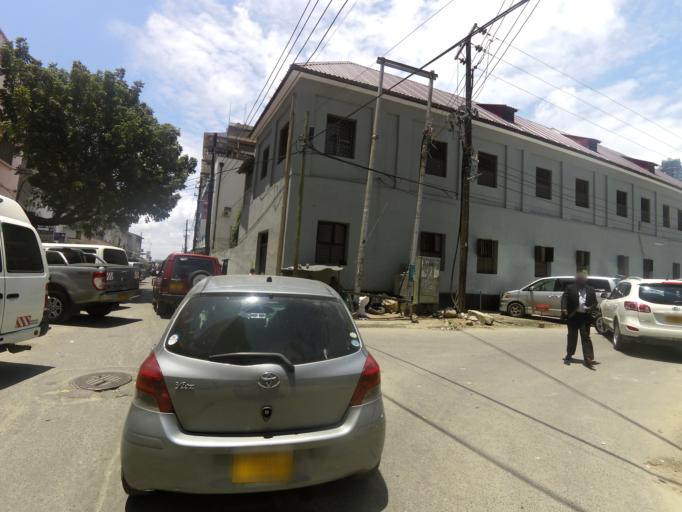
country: TZ
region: Dar es Salaam
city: Dar es Salaam
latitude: -6.8178
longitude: 39.2886
